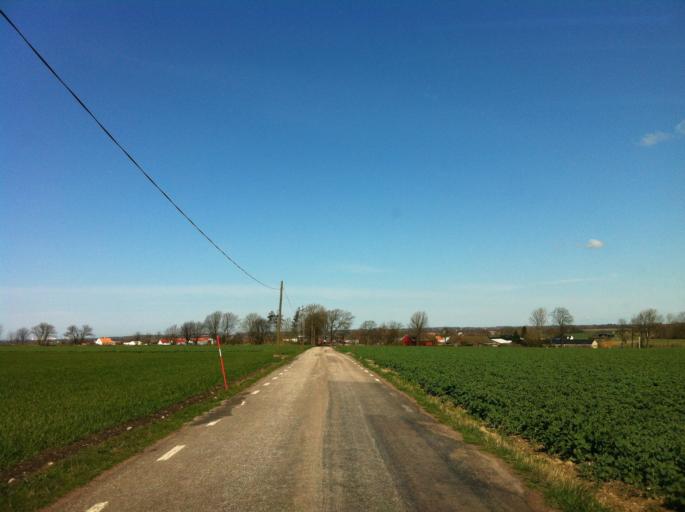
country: SE
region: Skane
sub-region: Helsingborg
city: Glumslov
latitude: 55.9419
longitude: 12.8408
